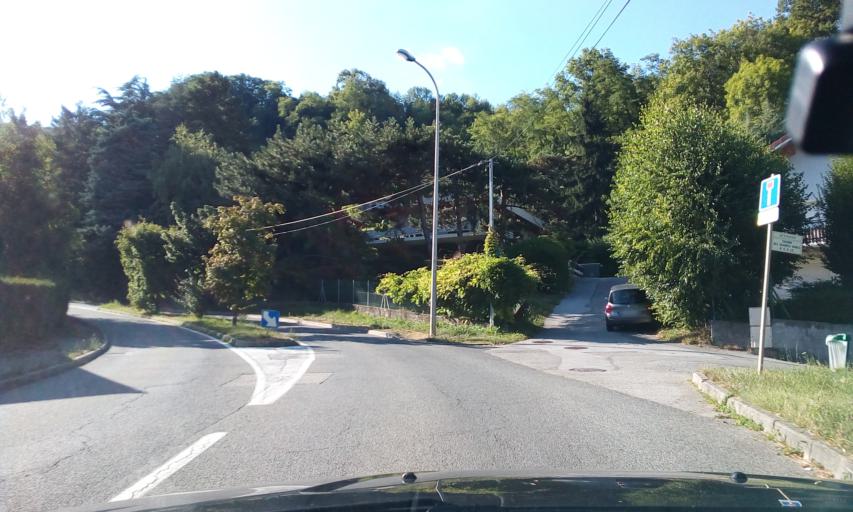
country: FR
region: Rhone-Alpes
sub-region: Departement de l'Isere
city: Seyssins
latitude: 45.1596
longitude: 5.6770
